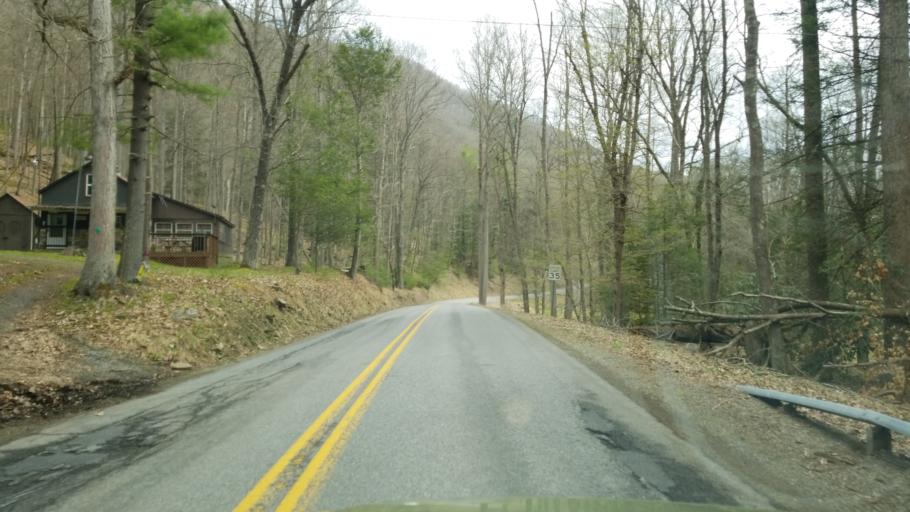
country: US
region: Pennsylvania
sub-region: Cameron County
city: Emporium
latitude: 41.2930
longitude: -78.1175
